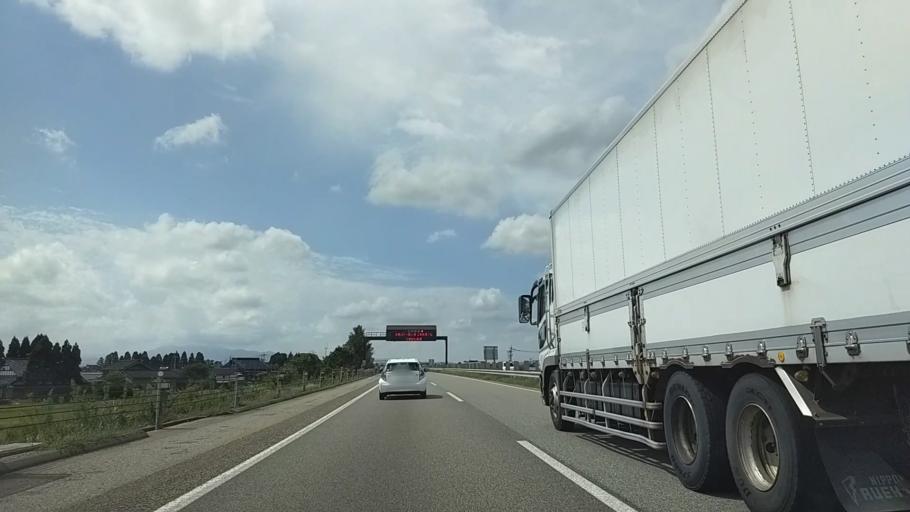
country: JP
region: Toyama
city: Takaoka
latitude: 36.6541
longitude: 136.9960
